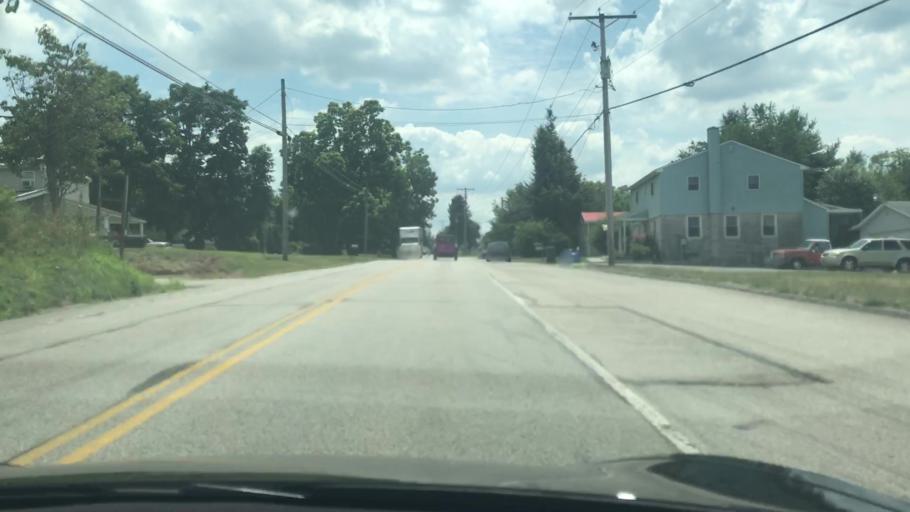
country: US
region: Pennsylvania
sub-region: York County
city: Manchester
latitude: 40.0573
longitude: -76.7657
